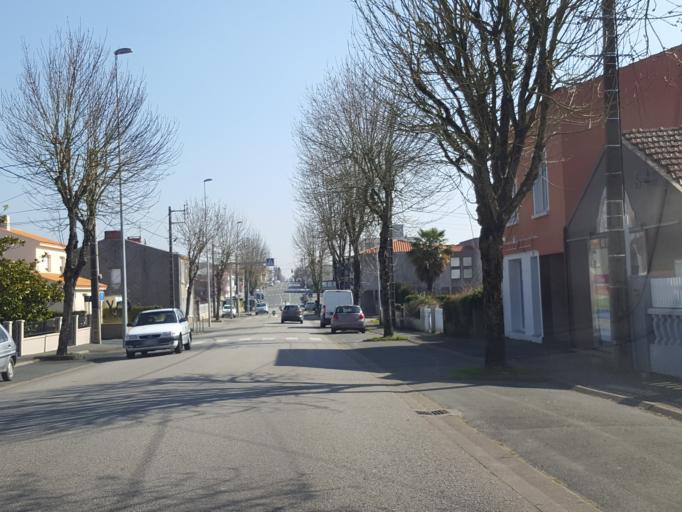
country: FR
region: Pays de la Loire
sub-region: Departement de la Vendee
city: La Roche-sur-Yon
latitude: 46.6609
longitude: -1.4060
